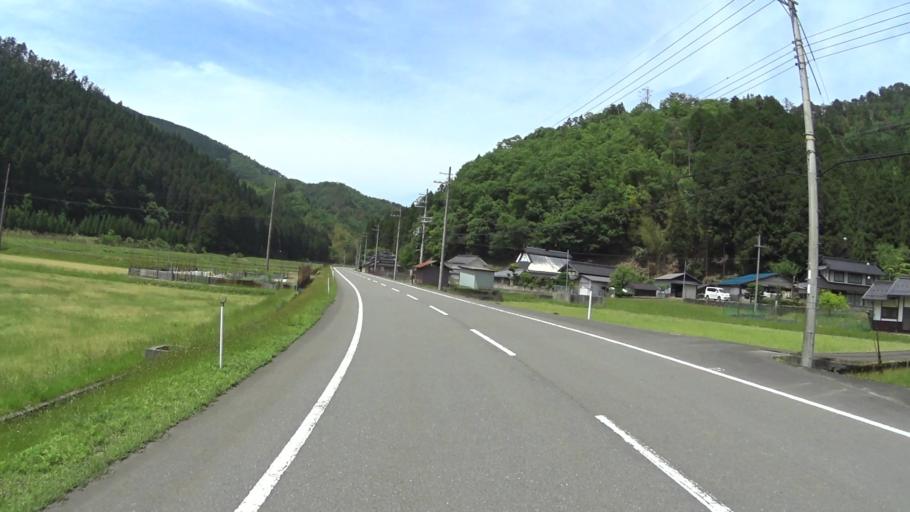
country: JP
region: Kyoto
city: Maizuru
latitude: 35.3955
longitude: 135.4636
